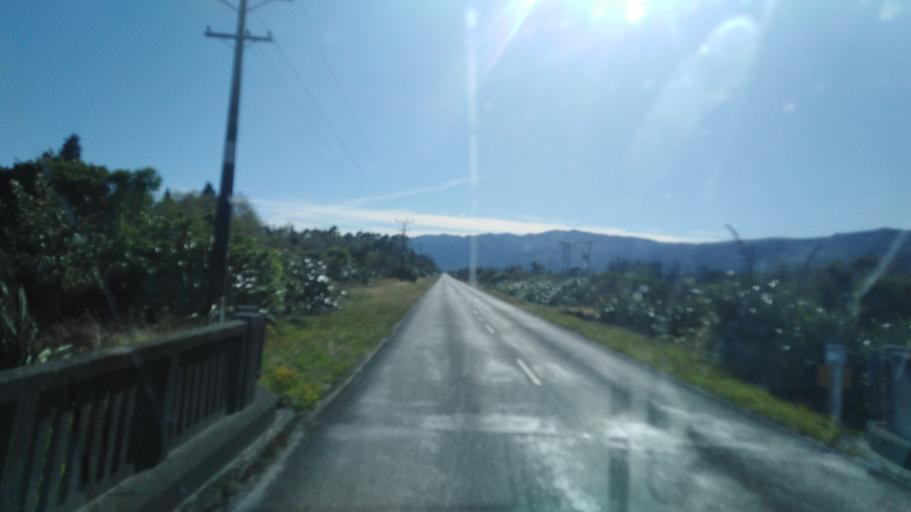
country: NZ
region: West Coast
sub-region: Buller District
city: Westport
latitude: -41.7449
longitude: 171.6865
